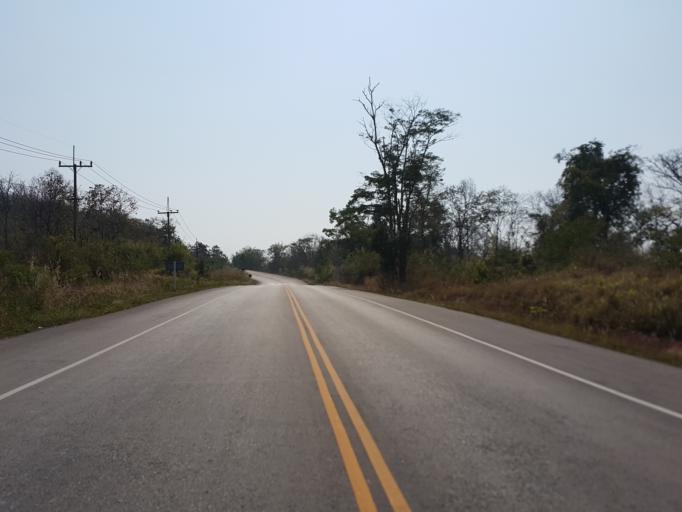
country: TH
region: Lampang
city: Mueang Pan
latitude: 18.8818
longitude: 99.6023
